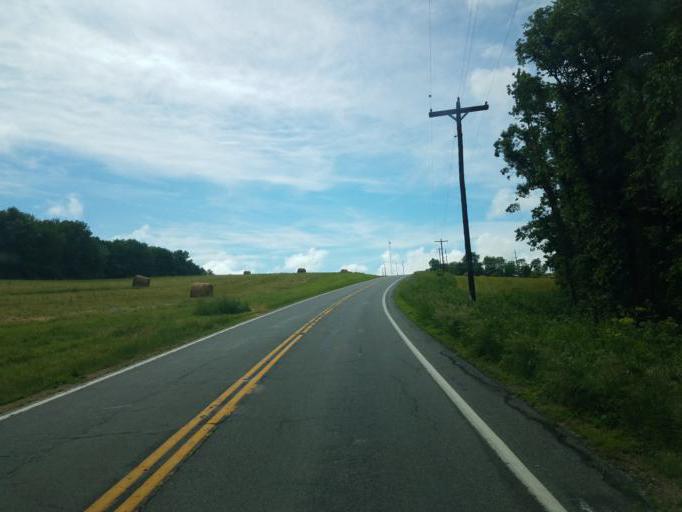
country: US
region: Wisconsin
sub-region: Vernon County
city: Hillsboro
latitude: 43.6662
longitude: -90.4526
